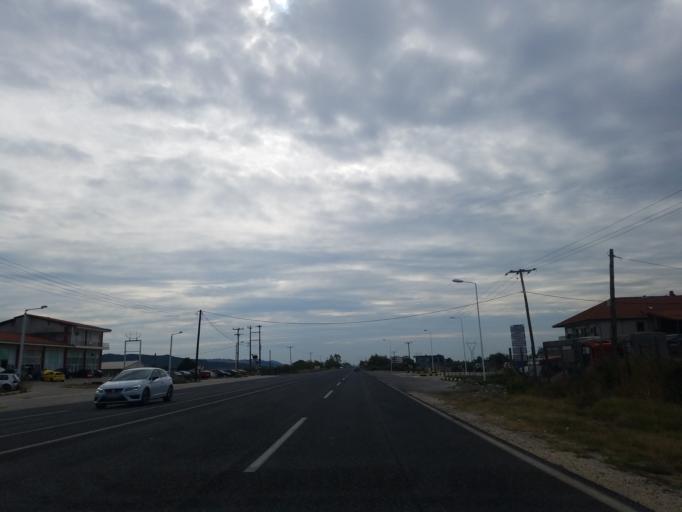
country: GR
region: Thessaly
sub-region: Trikala
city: Kalampaka
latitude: 39.6793
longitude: 21.6566
